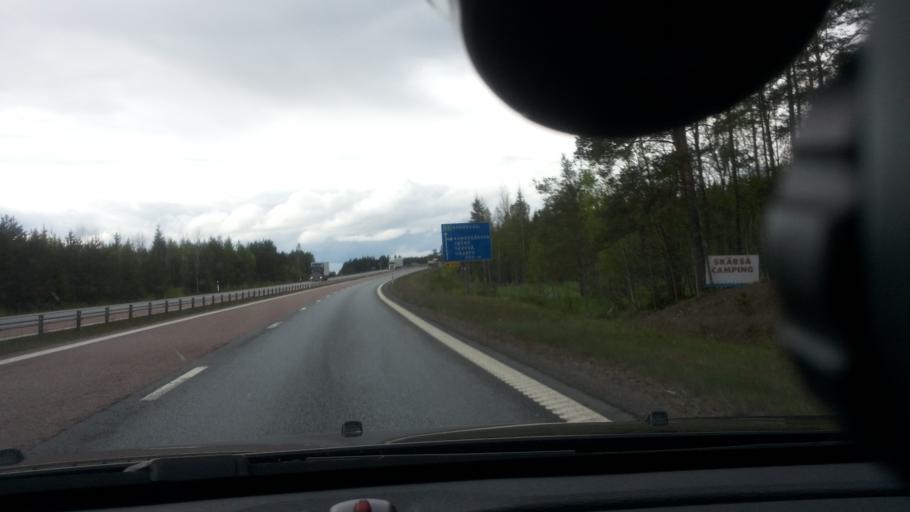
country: SE
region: Gaevleborg
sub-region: Soderhamns Kommun
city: Soderhamn
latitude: 61.3309
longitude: 17.0214
